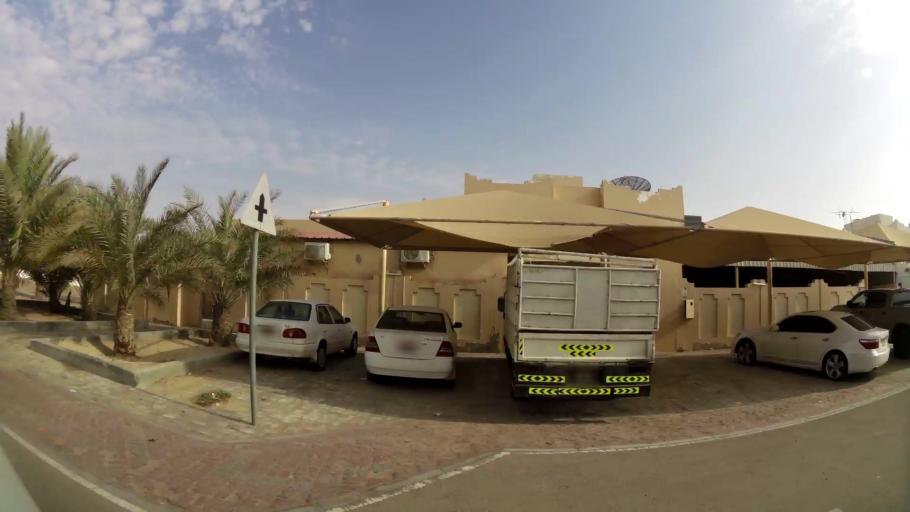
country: AE
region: Abu Dhabi
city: Abu Dhabi
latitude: 24.2388
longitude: 54.7236
